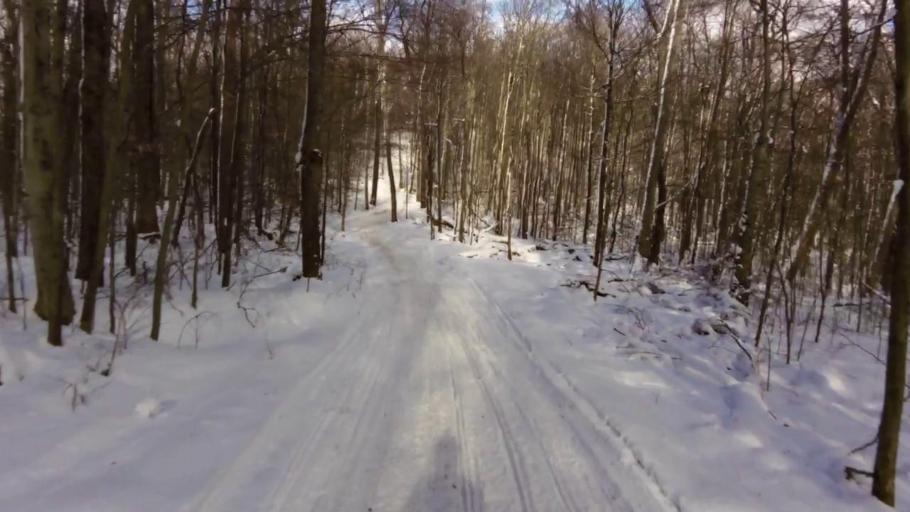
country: US
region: New York
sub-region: Cattaraugus County
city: Salamanca
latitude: 42.0597
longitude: -78.6996
